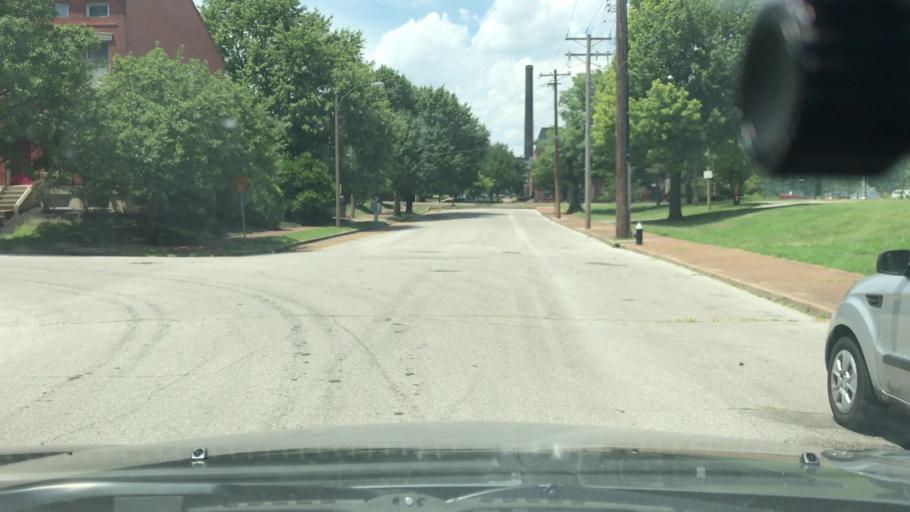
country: US
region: Missouri
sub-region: City of Saint Louis
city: St. Louis
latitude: 38.6130
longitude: -90.2044
